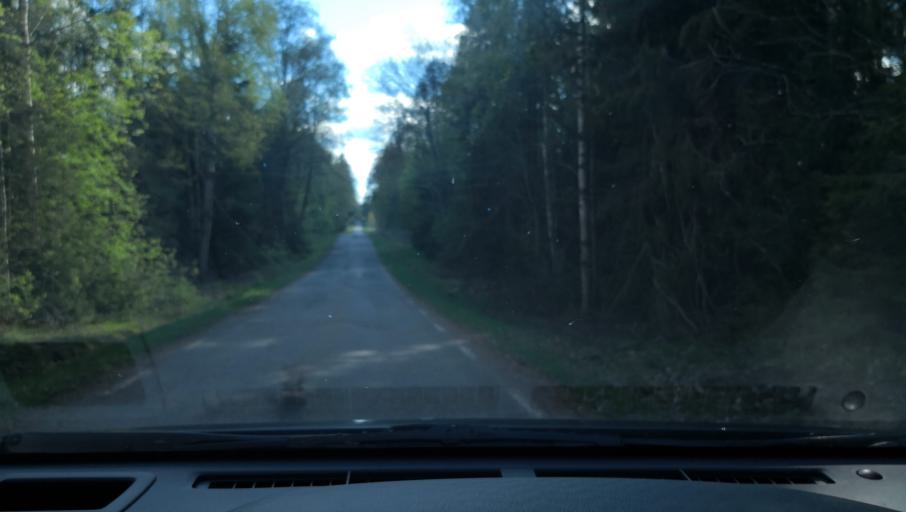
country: SE
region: OErebro
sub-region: Askersunds Kommun
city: Asbro
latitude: 58.9525
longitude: 15.0528
